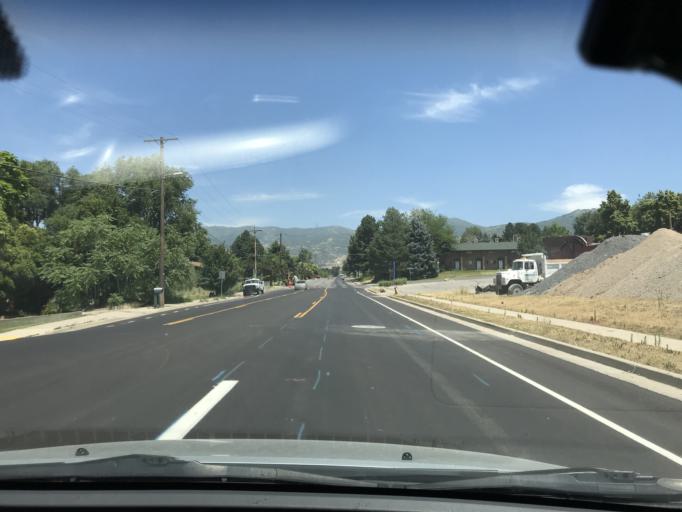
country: US
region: Utah
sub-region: Davis County
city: North Salt Lake
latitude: 40.8536
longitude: -111.8951
